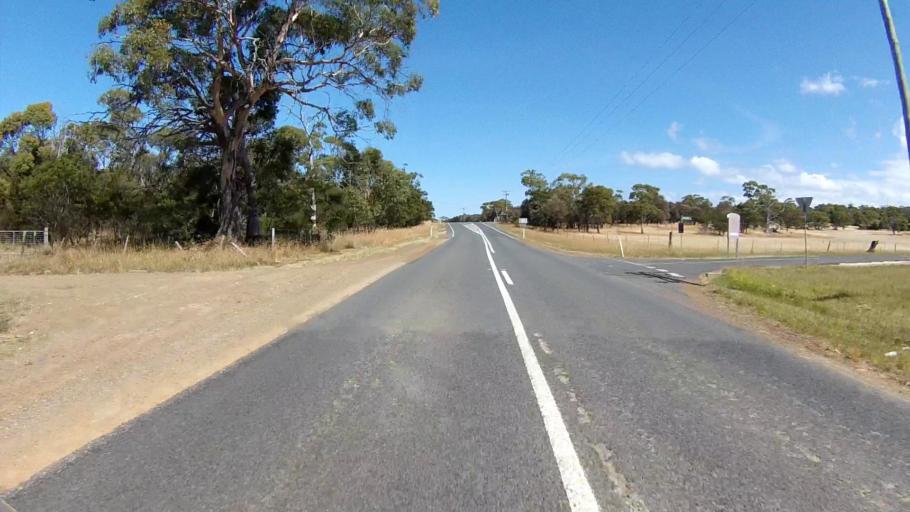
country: AU
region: Tasmania
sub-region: Sorell
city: Sorell
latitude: -42.1416
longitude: 148.0694
